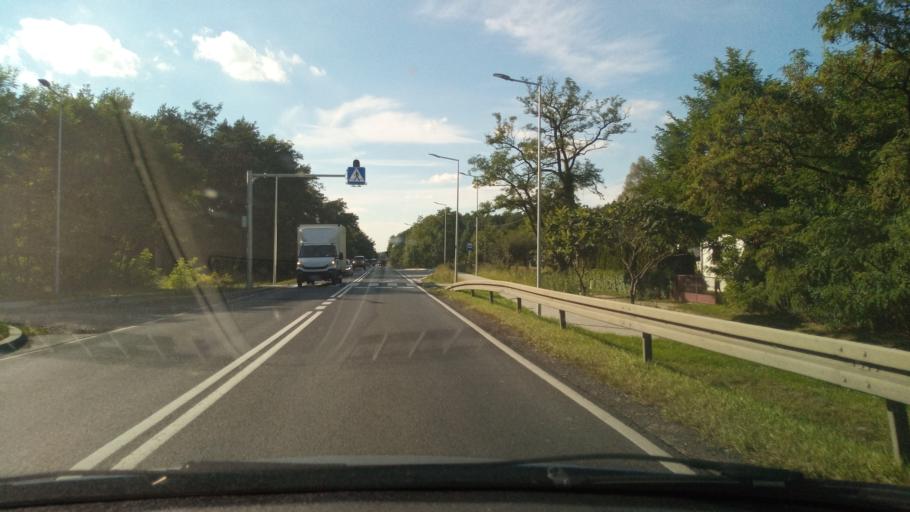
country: PL
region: Lodz Voivodeship
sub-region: Powiat piotrkowski
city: Sulejow
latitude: 51.3673
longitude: 19.8448
